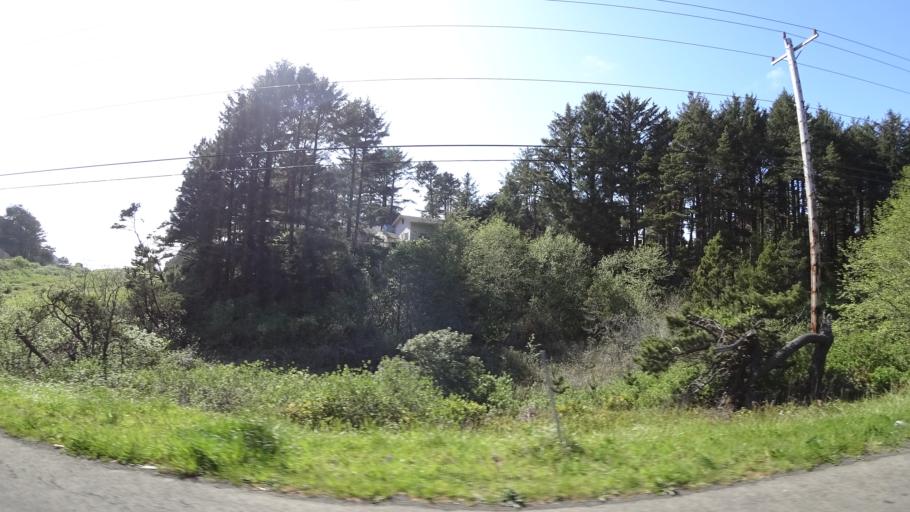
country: US
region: Oregon
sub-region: Lincoln County
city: Newport
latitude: 44.5739
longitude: -124.0667
